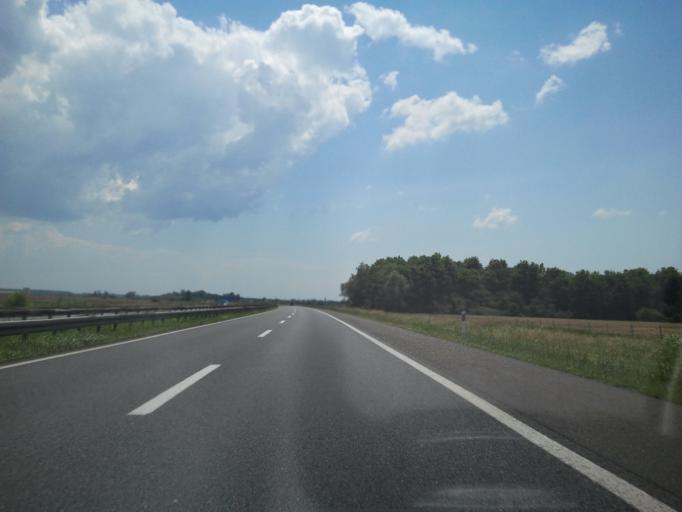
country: HR
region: Zagrebacka
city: Novoselec
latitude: 45.5826
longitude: 16.5614
